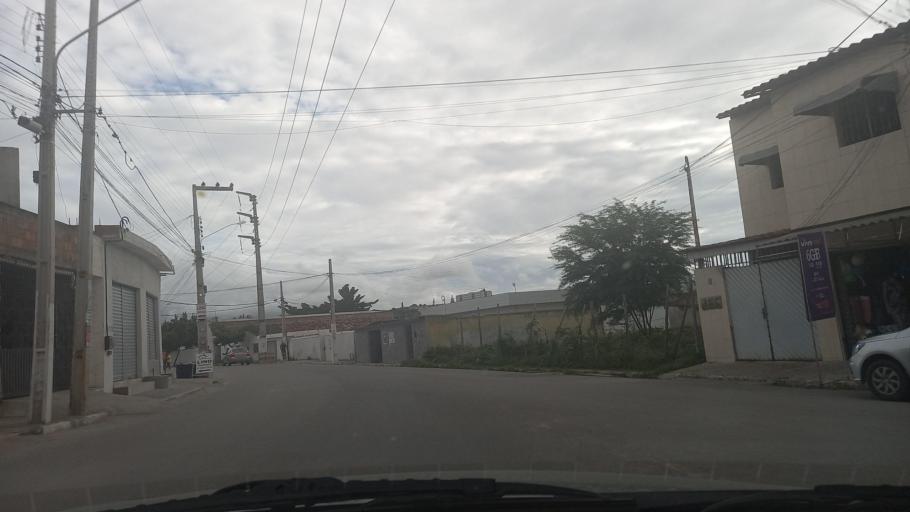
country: BR
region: Pernambuco
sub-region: Caruaru
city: Caruaru
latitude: -8.2955
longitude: -35.9832
